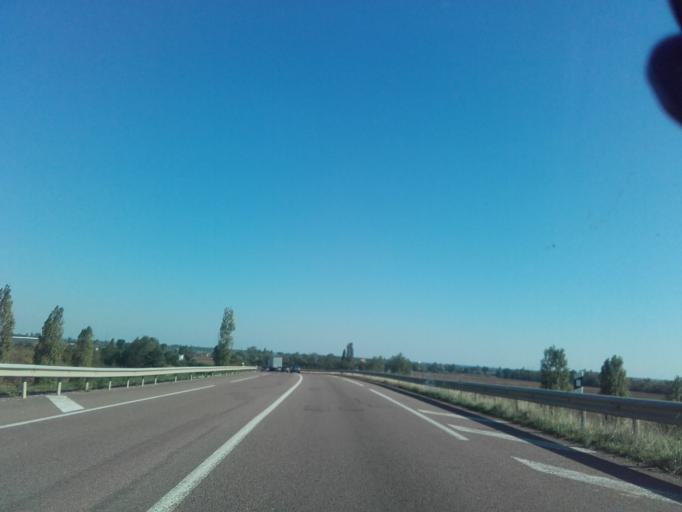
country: FR
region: Bourgogne
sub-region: Departement de la Cote-d'Or
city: Bligny-les-Beaune
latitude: 47.0038
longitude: 4.8302
